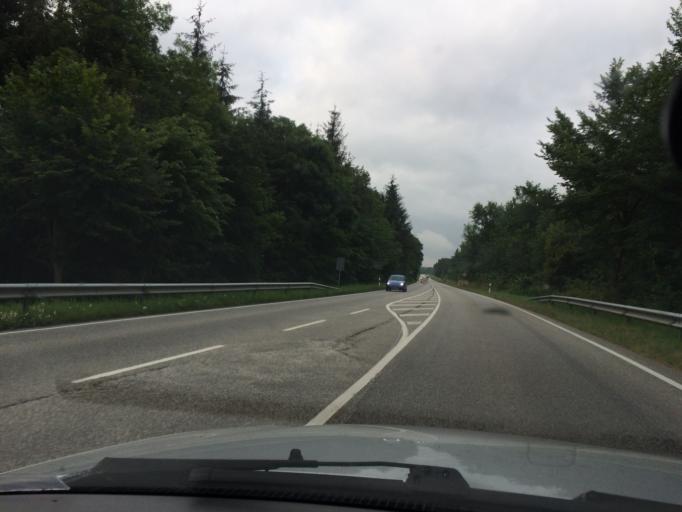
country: DE
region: Schleswig-Holstein
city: Oeversee
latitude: 54.6919
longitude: 9.4315
